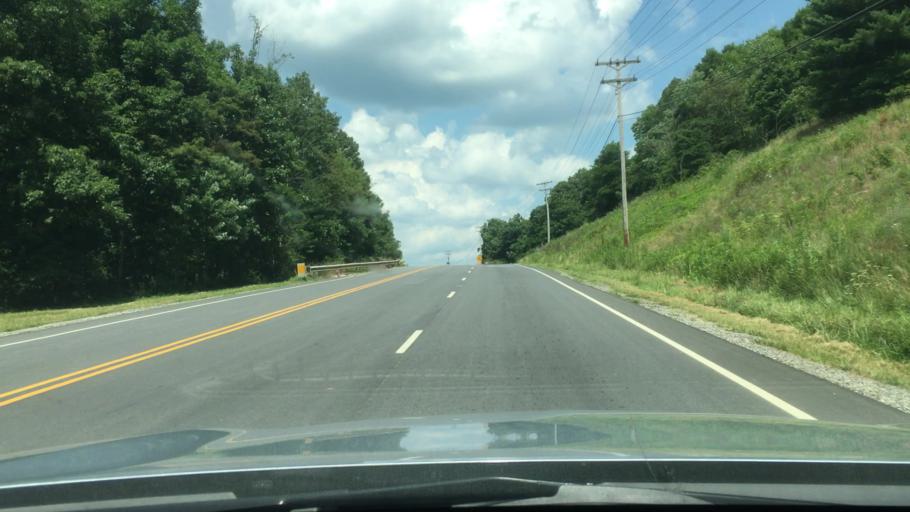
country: US
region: North Carolina
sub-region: Madison County
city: Marshall
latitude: 35.8209
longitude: -82.6364
